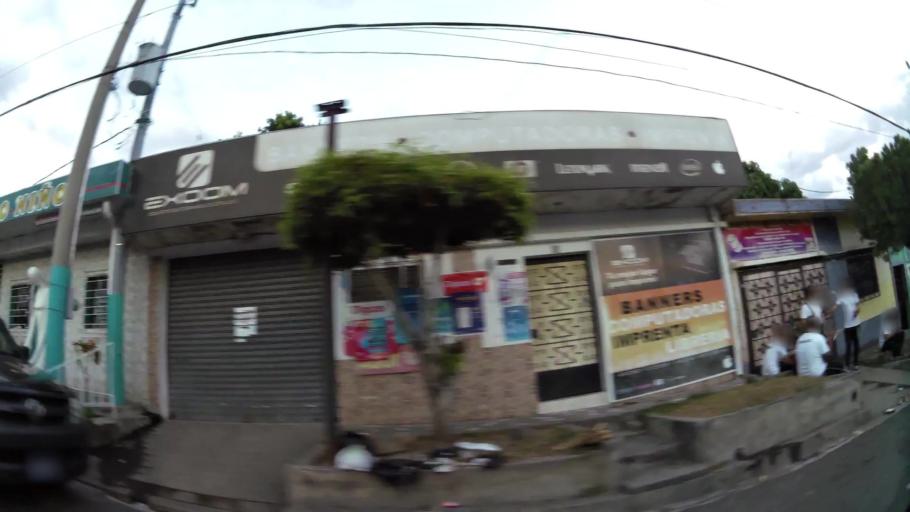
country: SV
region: San Vicente
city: San Vicente
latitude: 13.6424
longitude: -88.7899
